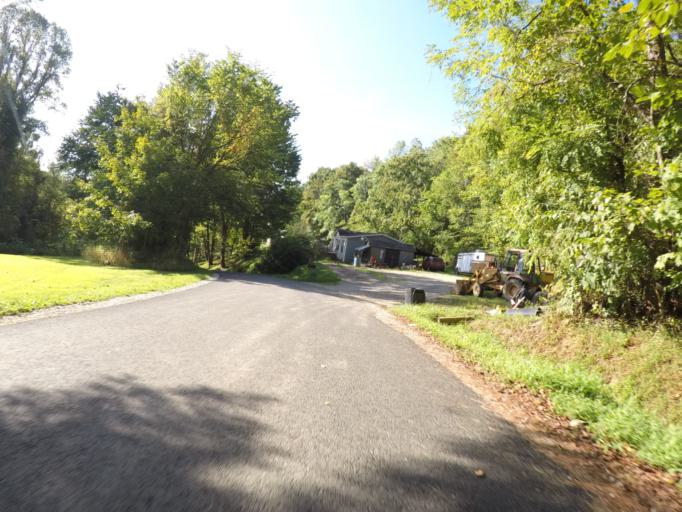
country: US
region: Ohio
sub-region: Lawrence County
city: Burlington
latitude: 38.5211
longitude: -82.5298
